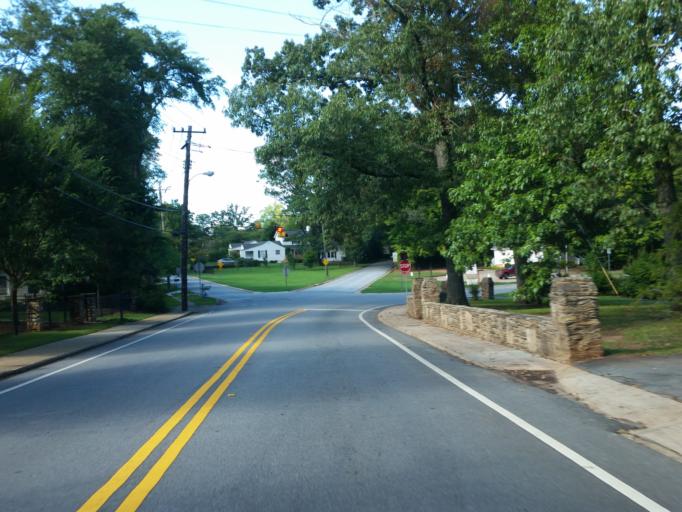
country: US
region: Georgia
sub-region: Cobb County
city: Smyrna
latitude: 33.8875
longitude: -84.5120
